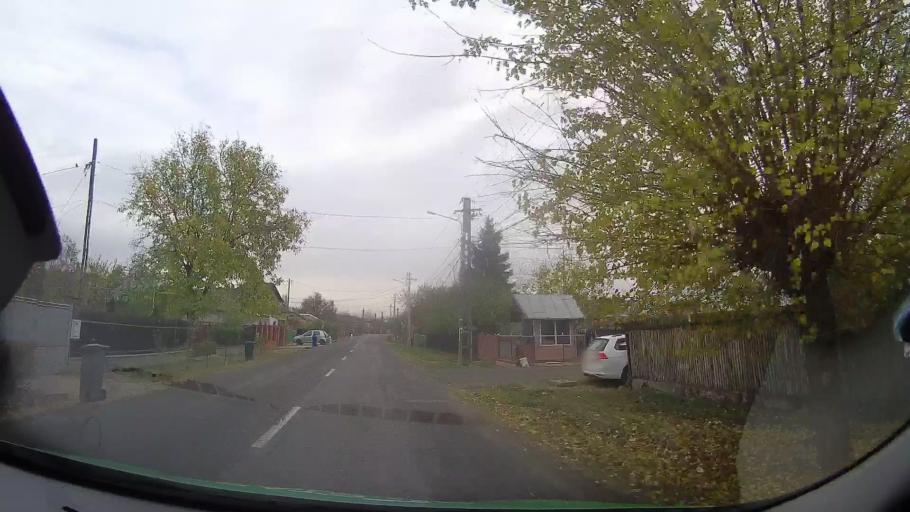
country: RO
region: Prahova
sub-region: Comuna Berceni
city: Berceni
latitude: 44.9341
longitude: 26.1224
